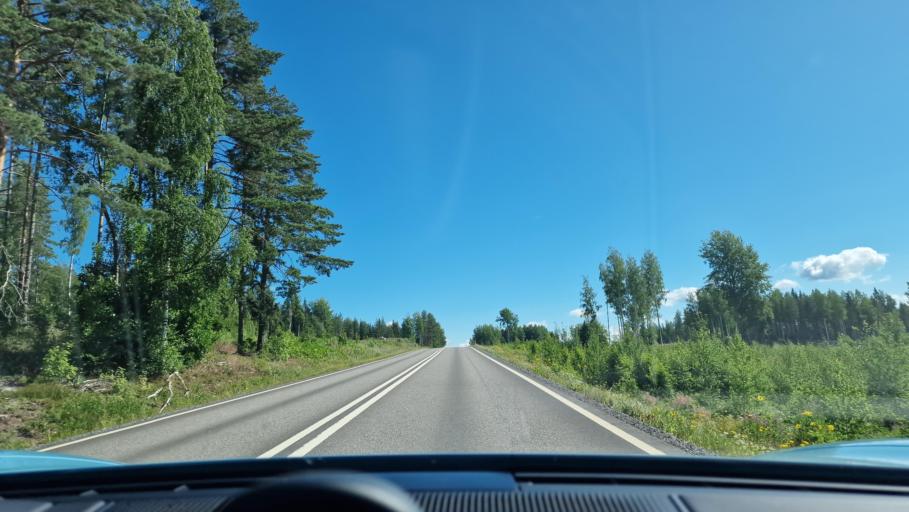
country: FI
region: Pirkanmaa
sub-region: Tampere
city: Kangasala
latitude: 61.4986
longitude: 24.1700
